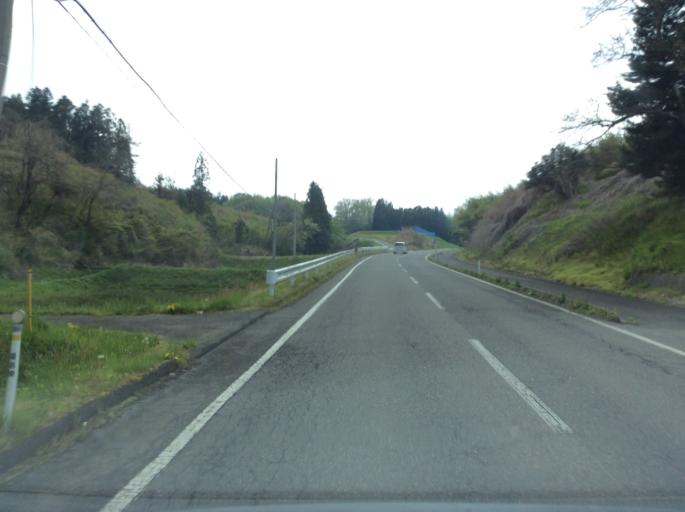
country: JP
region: Fukushima
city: Miharu
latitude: 37.4017
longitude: 140.5356
